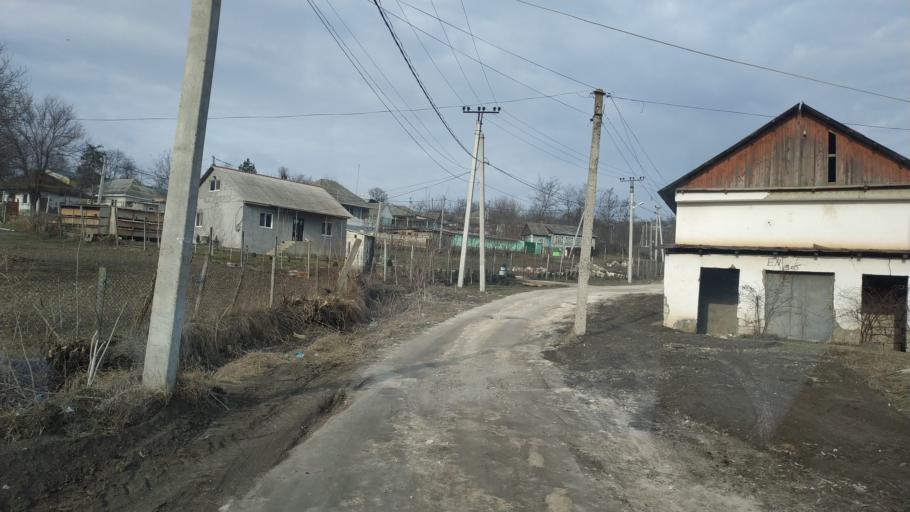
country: MD
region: Chisinau
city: Vadul lui Voda
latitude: 47.0107
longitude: 29.1318
